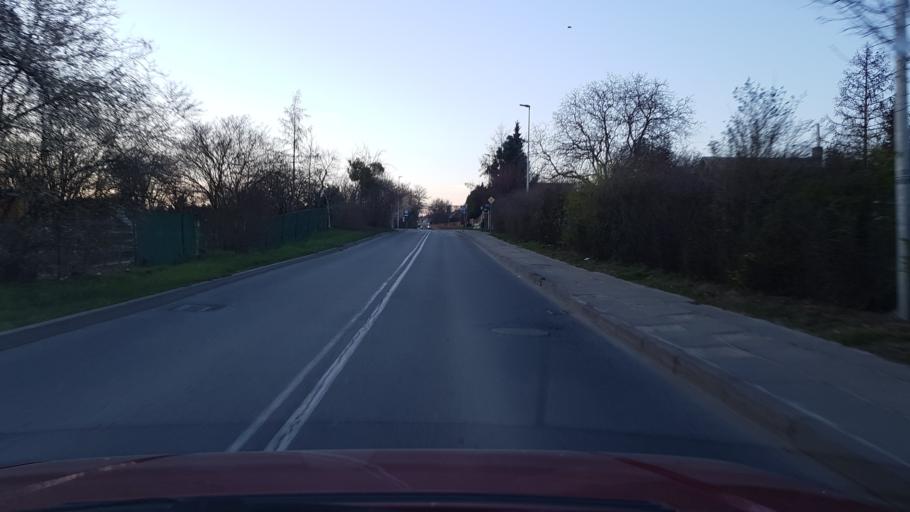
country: PL
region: West Pomeranian Voivodeship
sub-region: Szczecin
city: Szczecin
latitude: 53.4654
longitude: 14.5532
